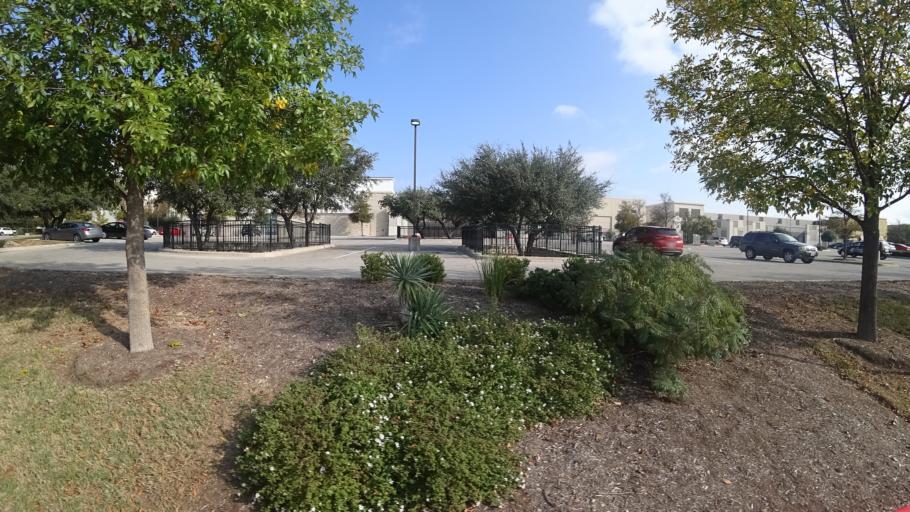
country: US
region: Texas
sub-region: Travis County
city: Bee Cave
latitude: 30.3090
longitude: -97.9431
